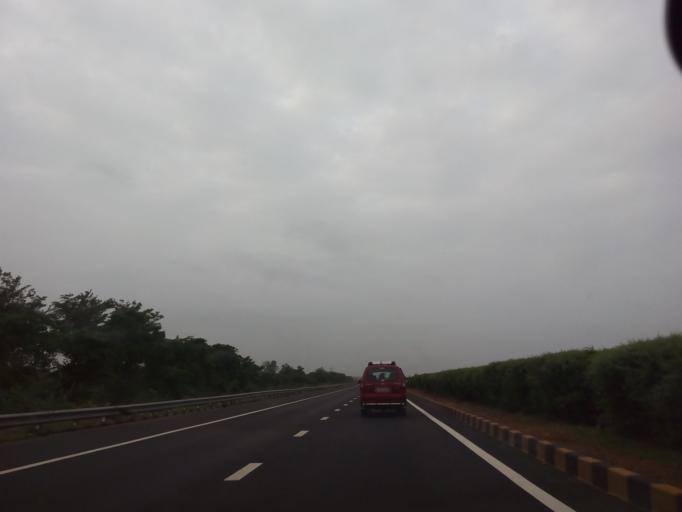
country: IN
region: Gujarat
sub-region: Kheda
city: Nadiad
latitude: 22.7744
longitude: 72.8492
